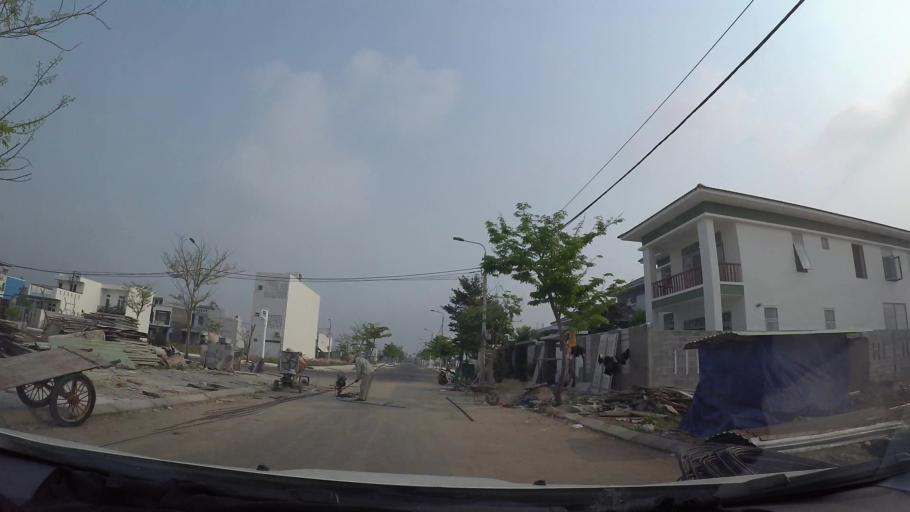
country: VN
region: Da Nang
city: Ngu Hanh Son
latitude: 16.0104
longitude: 108.2306
